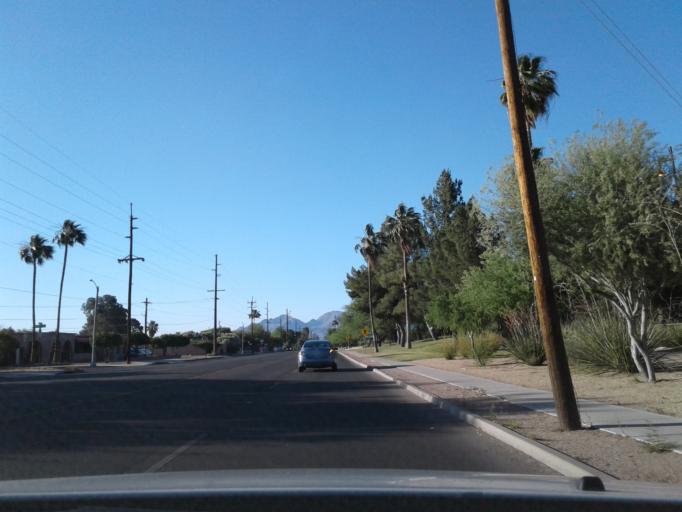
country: US
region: Arizona
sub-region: Pima County
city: Tucson
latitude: 32.2100
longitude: -110.9266
